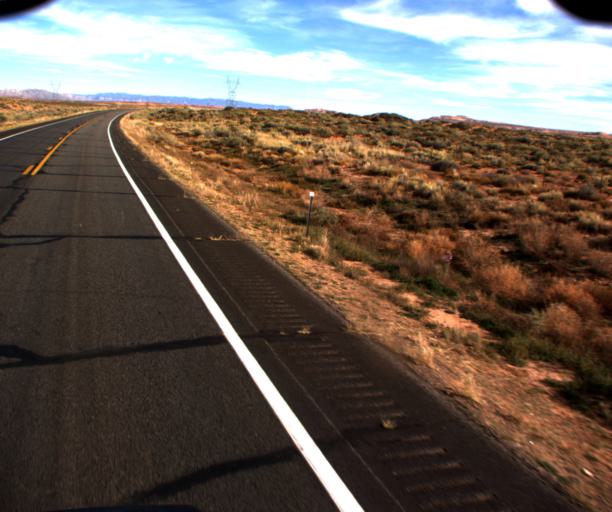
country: US
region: Arizona
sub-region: Apache County
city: Many Farms
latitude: 36.9413
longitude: -109.6463
